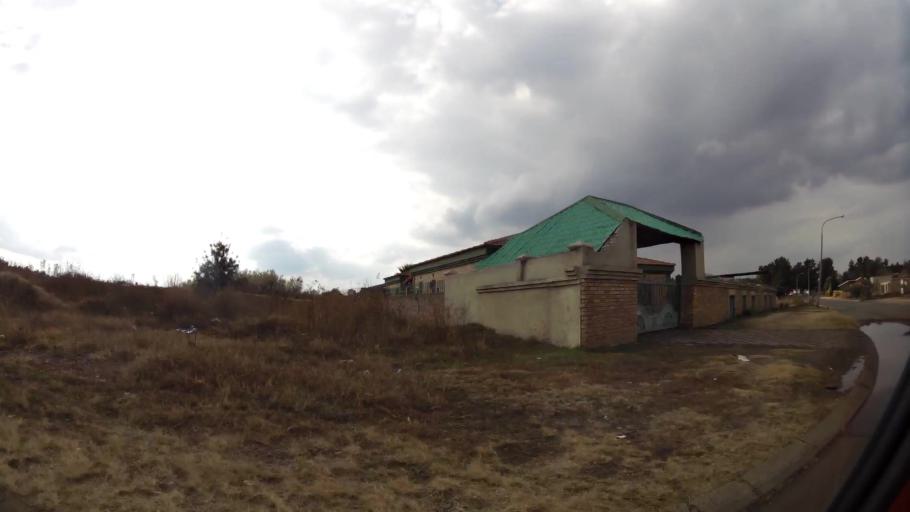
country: ZA
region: Gauteng
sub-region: Sedibeng District Municipality
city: Vanderbijlpark
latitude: -26.7085
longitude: 27.8004
